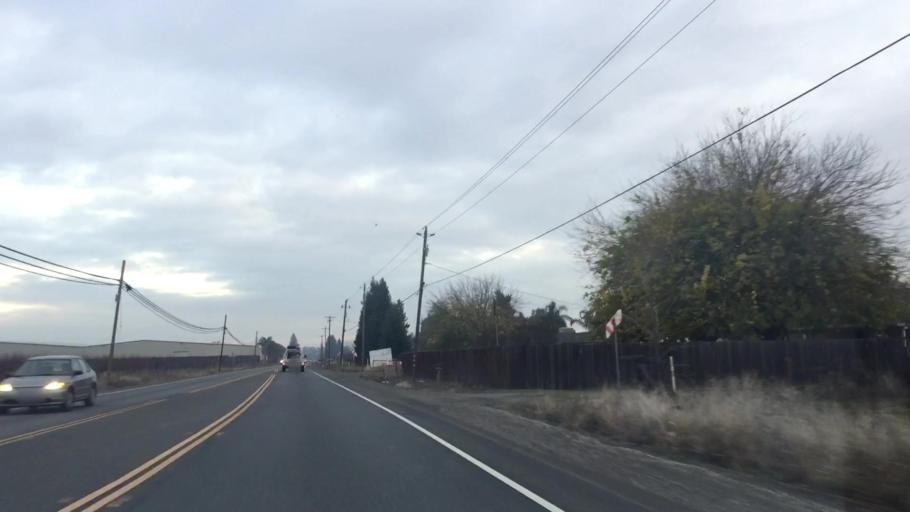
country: US
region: California
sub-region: Yuba County
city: Marysville
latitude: 39.1816
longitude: -121.5923
